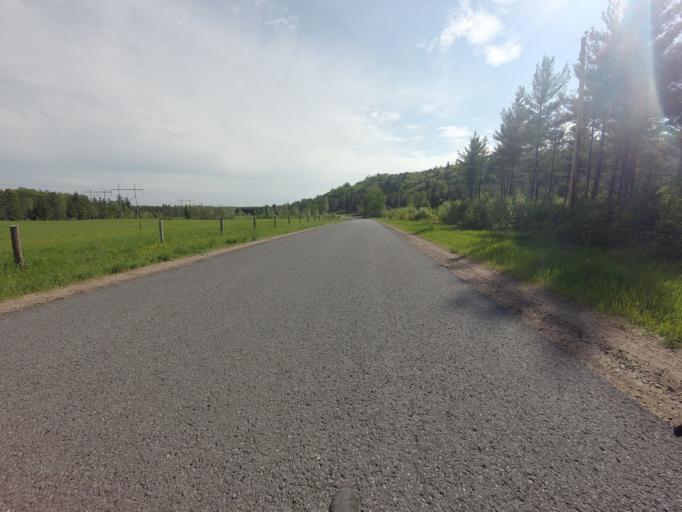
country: US
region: New York
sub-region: St. Lawrence County
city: Gouverneur
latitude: 44.2200
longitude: -75.2390
